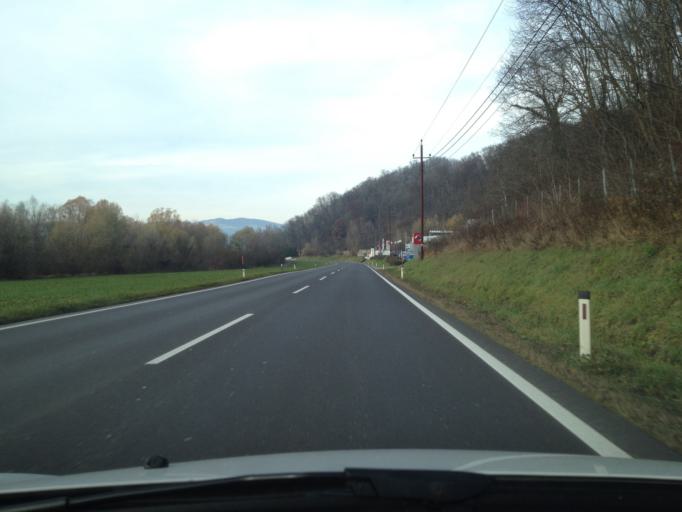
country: AT
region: Upper Austria
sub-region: Politischer Bezirk Urfahr-Umgebung
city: Steyregg
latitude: 48.3005
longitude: 14.3419
